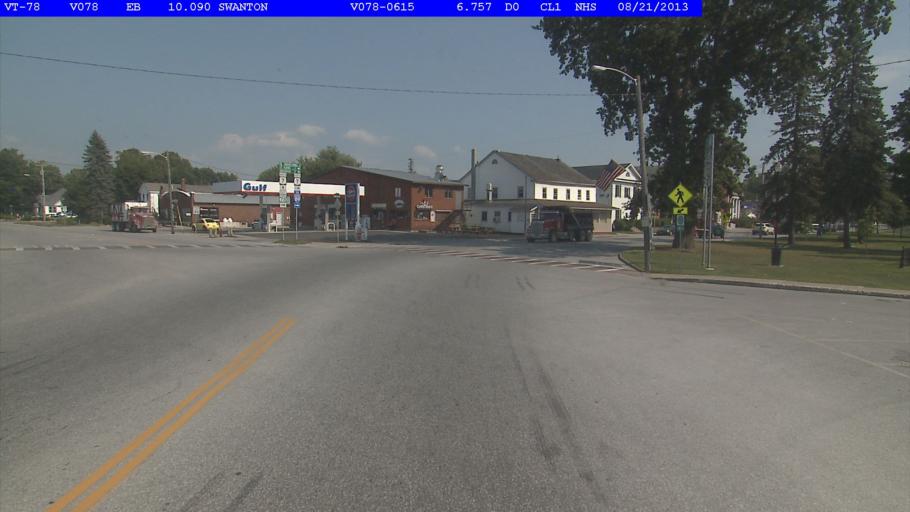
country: US
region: Vermont
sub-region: Franklin County
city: Swanton
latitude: 44.9194
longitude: -73.1257
